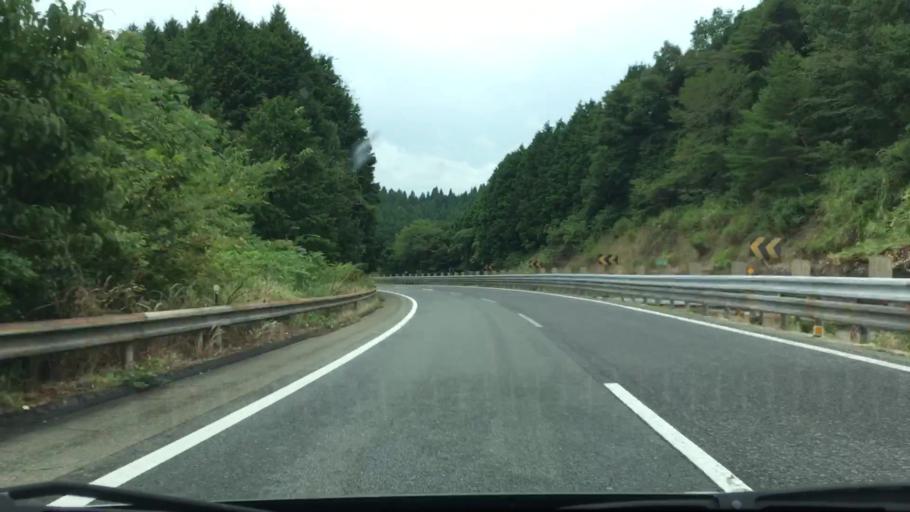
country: JP
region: Hiroshima
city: Shobara
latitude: 34.8839
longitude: 133.1941
